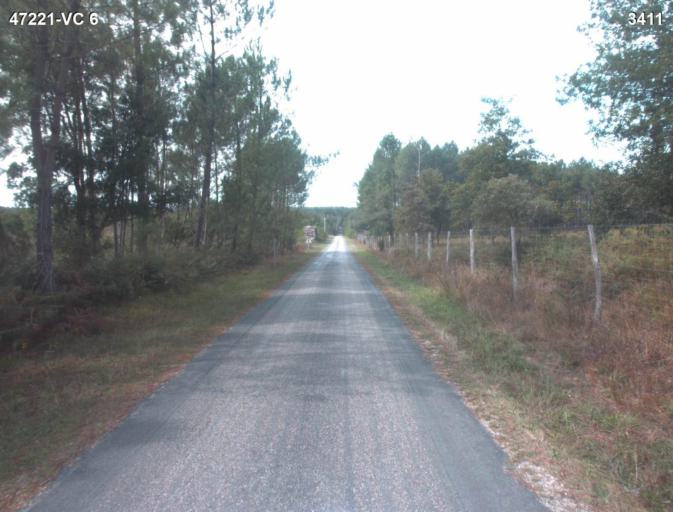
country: FR
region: Aquitaine
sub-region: Departement du Lot-et-Garonne
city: Mezin
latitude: 44.1088
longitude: 0.1412
